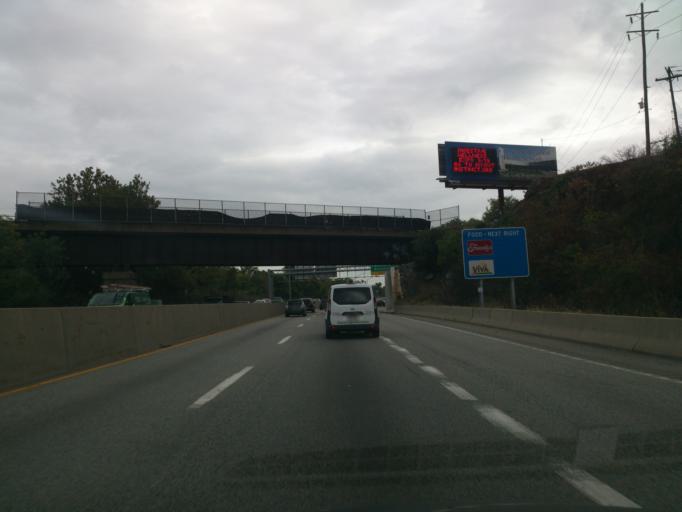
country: US
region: Pennsylvania
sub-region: Berks County
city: West Reading
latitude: 40.3470
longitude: -75.9541
